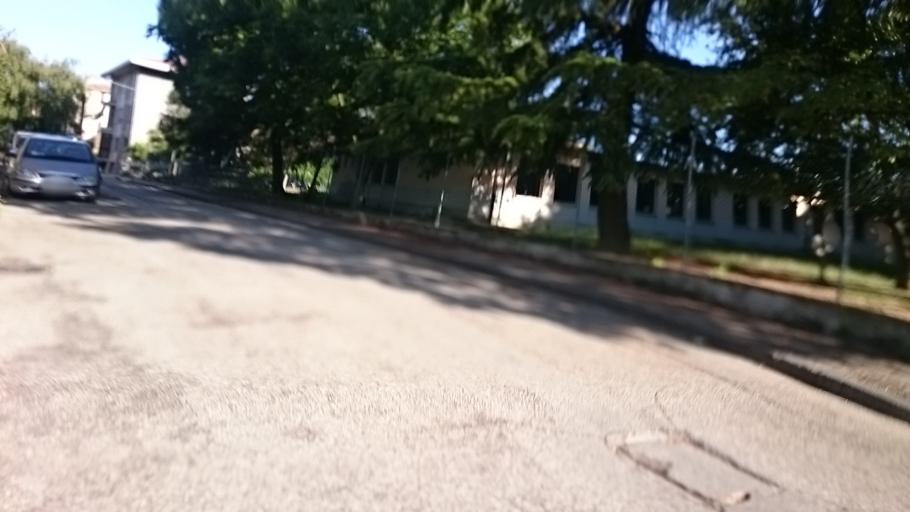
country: IT
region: Veneto
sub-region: Provincia di Padova
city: Mejaniga
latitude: 45.4431
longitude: 11.8975
